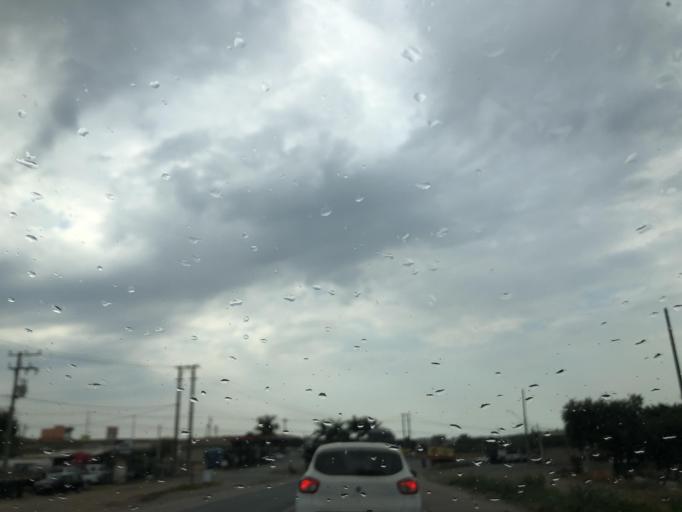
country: BR
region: Sao Paulo
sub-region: Salto De Pirapora
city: Salto de Pirapora
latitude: -23.6436
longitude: -47.5825
